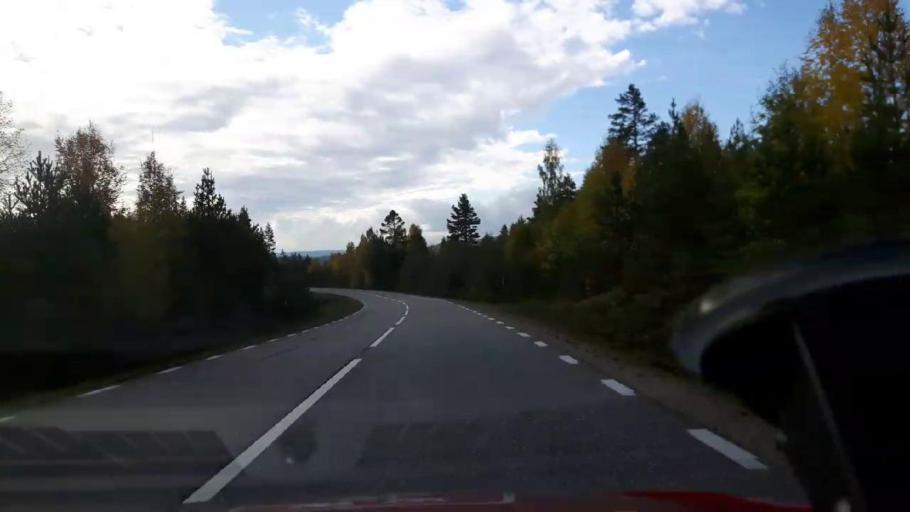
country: SE
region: Gaevleborg
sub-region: Ljusdals Kommun
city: Farila
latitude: 62.0026
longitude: 15.2400
